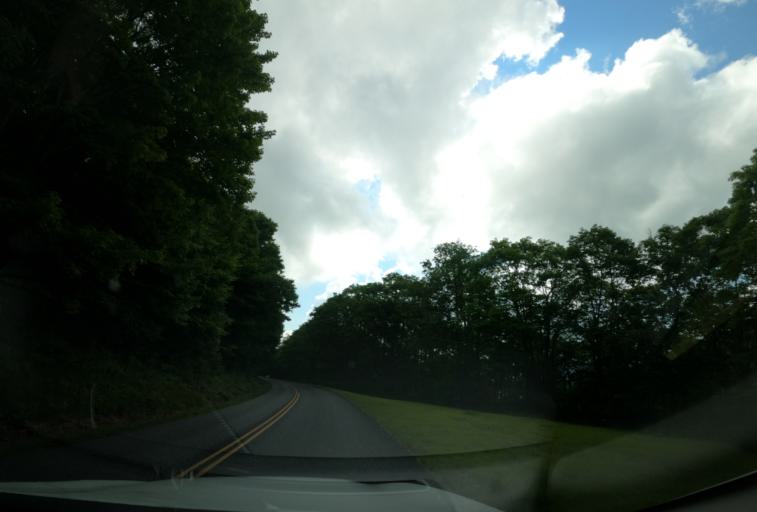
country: US
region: North Carolina
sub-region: Haywood County
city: Hazelwood
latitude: 35.4247
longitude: -83.0454
